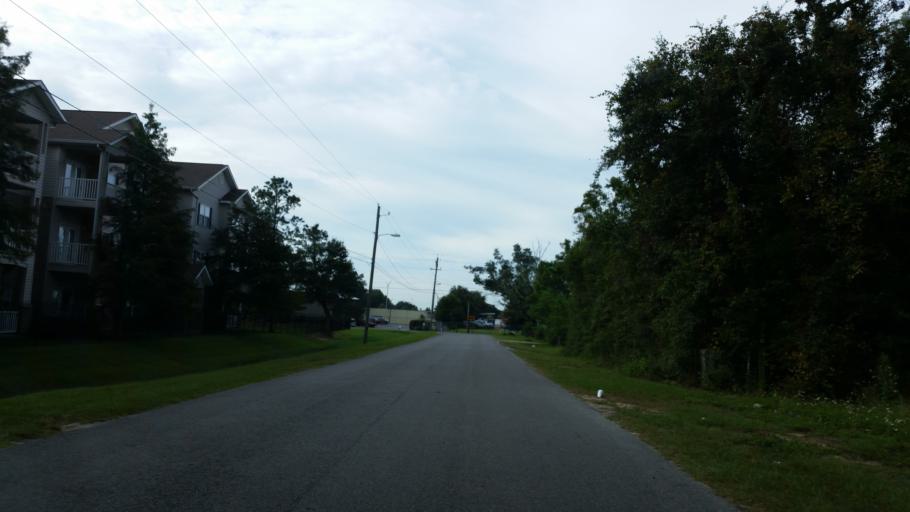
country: US
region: Florida
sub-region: Escambia County
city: Ferry Pass
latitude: 30.5062
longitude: -87.2249
